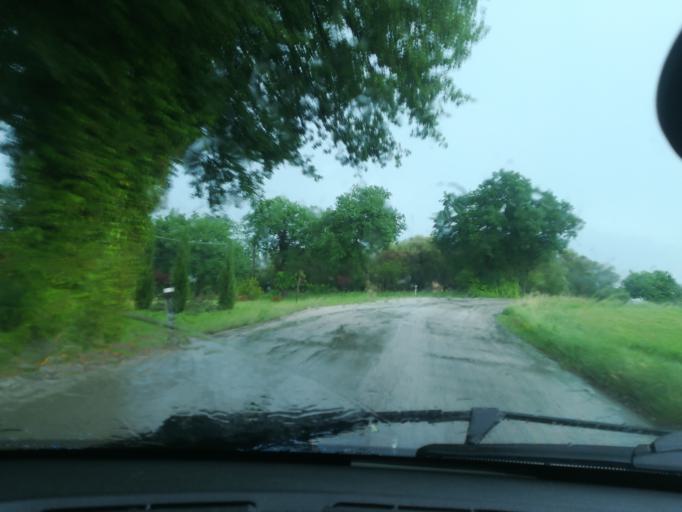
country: IT
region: The Marches
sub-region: Provincia di Macerata
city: Treia
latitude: 43.3077
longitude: 13.3287
